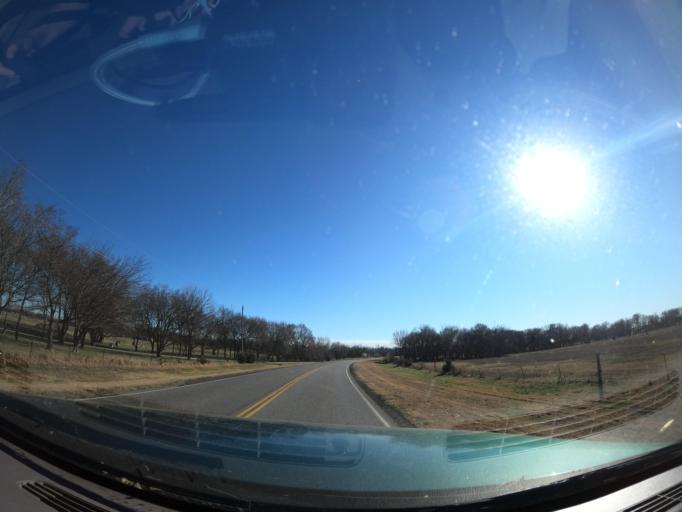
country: US
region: Oklahoma
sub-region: McIntosh County
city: Checotah
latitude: 35.5613
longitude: -95.6519
